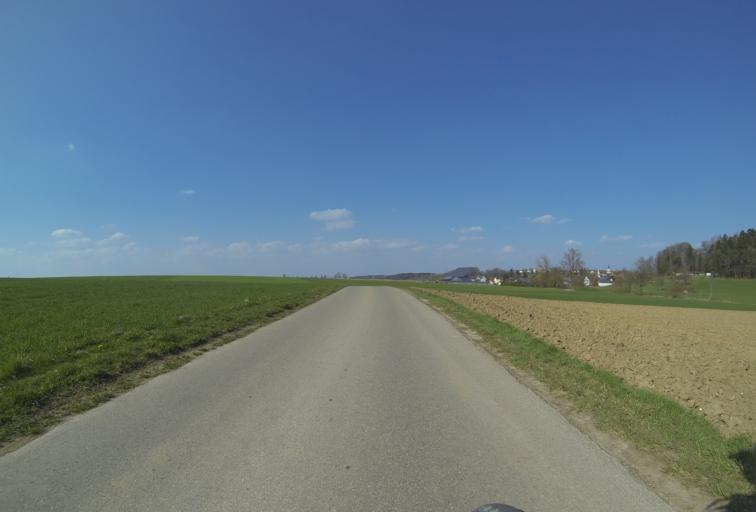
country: DE
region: Baden-Wuerttemberg
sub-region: Tuebingen Region
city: Huttisheim
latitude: 48.2555
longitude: 9.9516
